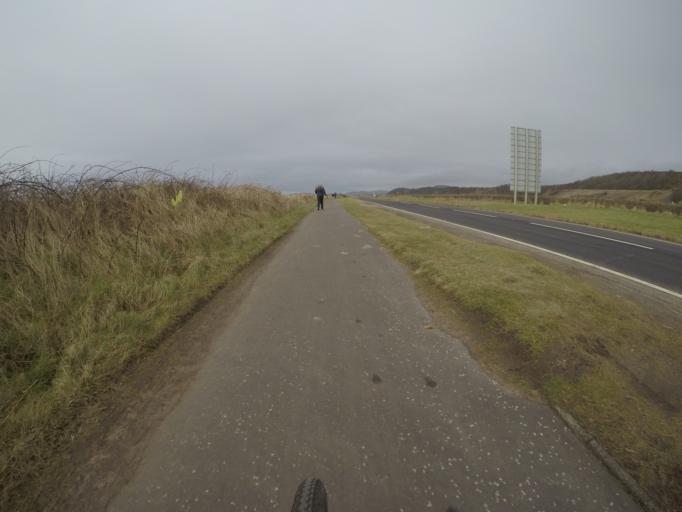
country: GB
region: Scotland
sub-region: North Ayrshire
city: Ardrossan
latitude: 55.6560
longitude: -4.8271
